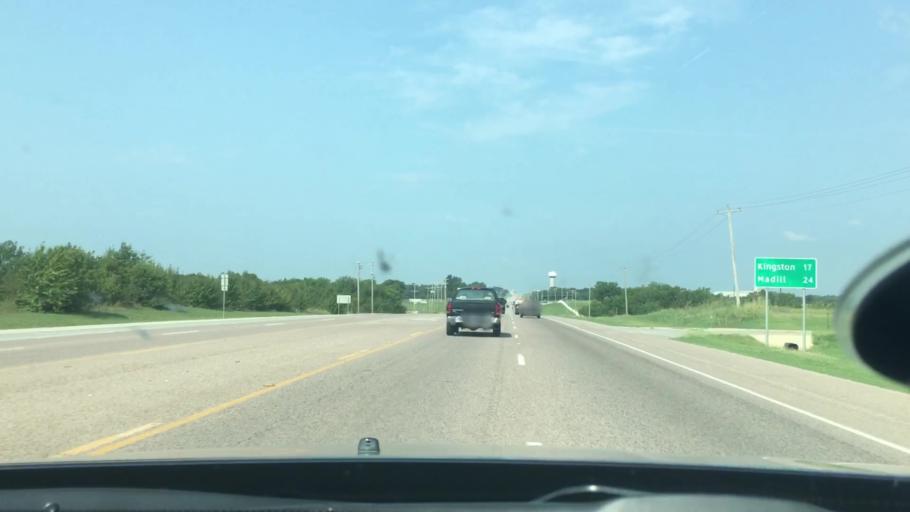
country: US
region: Oklahoma
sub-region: Bryan County
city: Durant
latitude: 33.9977
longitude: -96.4299
